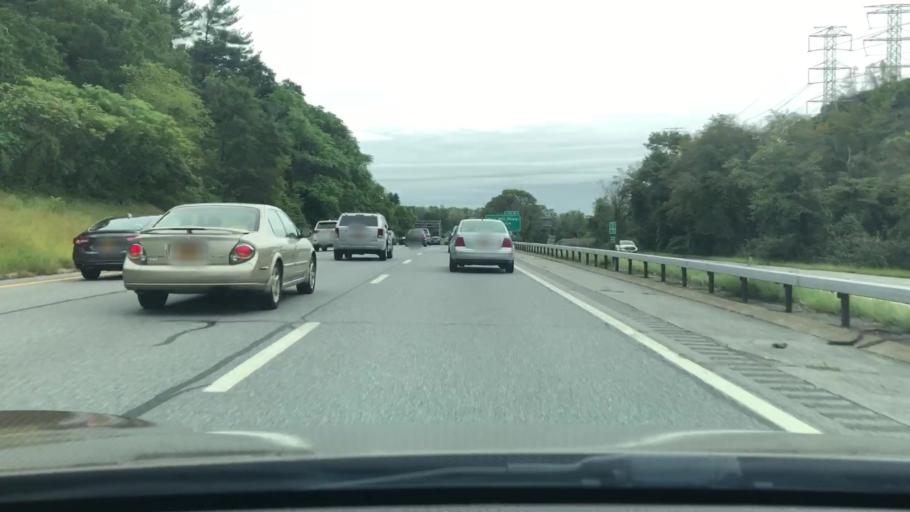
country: US
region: New York
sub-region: Westchester County
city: Hawthorne
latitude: 41.1210
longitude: -73.8085
